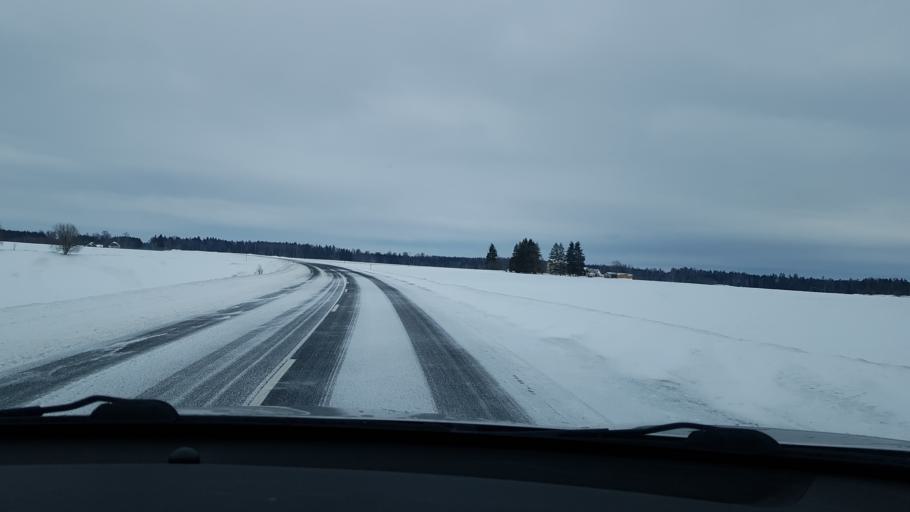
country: EE
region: Jaervamaa
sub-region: Jaerva-Jaani vald
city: Jarva-Jaani
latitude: 59.1124
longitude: 25.7959
